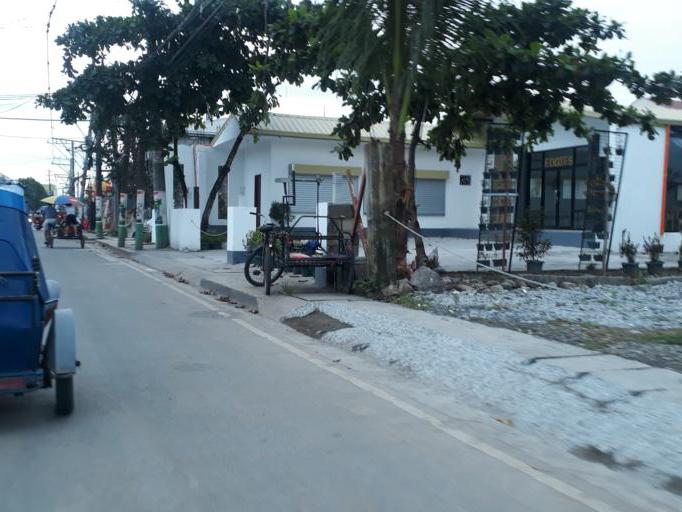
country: PH
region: Central Luzon
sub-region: Province of Bulacan
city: Obando
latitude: 14.7097
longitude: 120.9517
